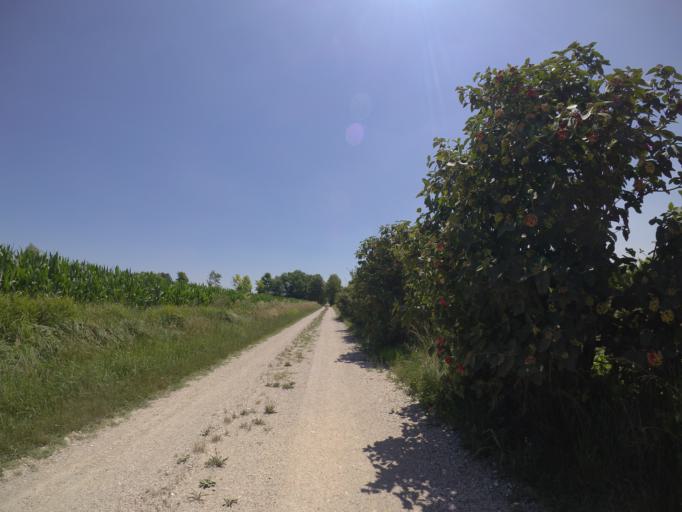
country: IT
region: Friuli Venezia Giulia
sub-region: Provincia di Udine
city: Bertiolo
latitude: 45.9419
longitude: 13.0165
